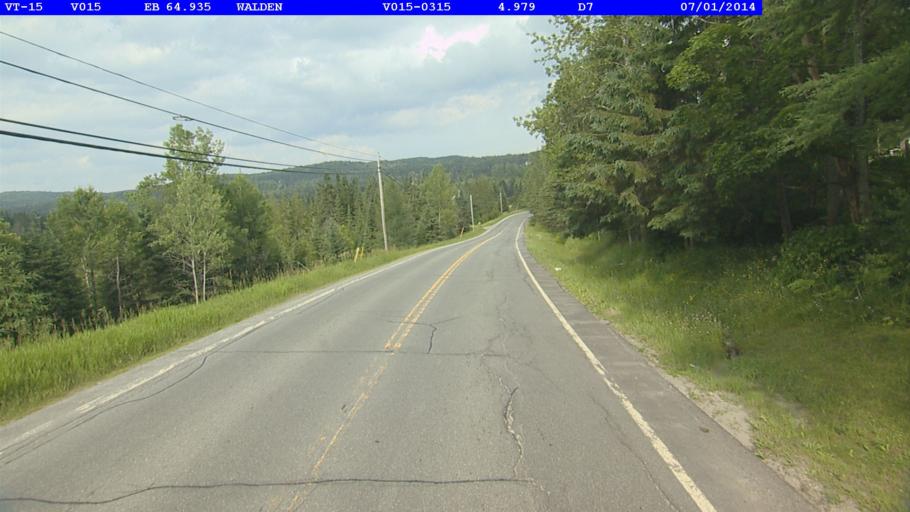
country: US
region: Vermont
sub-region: Caledonia County
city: Hardwick
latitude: 44.4496
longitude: -72.2287
